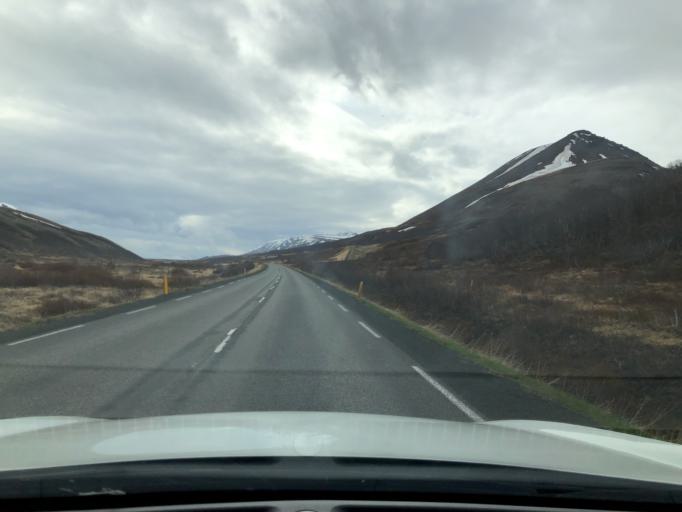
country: IS
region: Northeast
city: Akureyri
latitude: 65.7422
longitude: -17.8733
